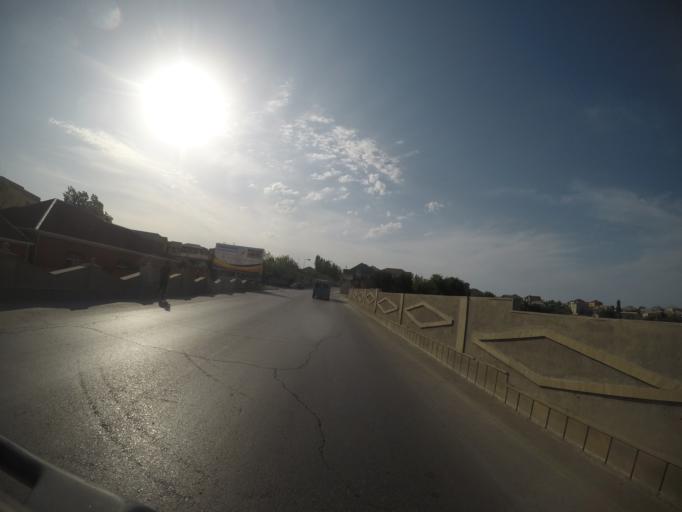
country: AZ
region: Baki
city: Binagadi
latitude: 40.4699
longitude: 49.8386
